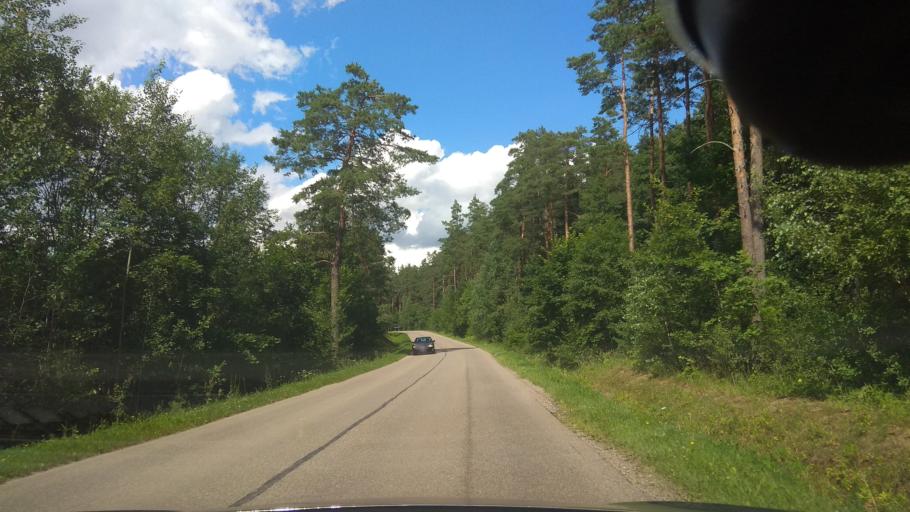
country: LT
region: Vilnius County
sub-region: Trakai
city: Rudiskes
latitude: 54.5132
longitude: 24.8476
